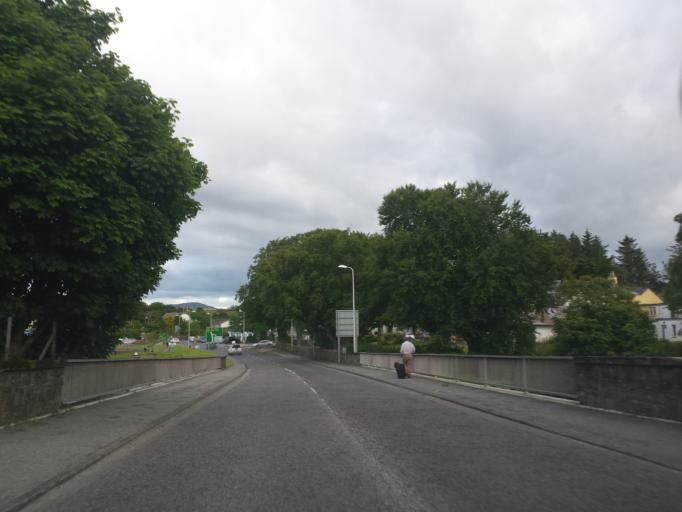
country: GB
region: Scotland
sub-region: Highland
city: Portree
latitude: 57.2426
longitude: -5.9129
